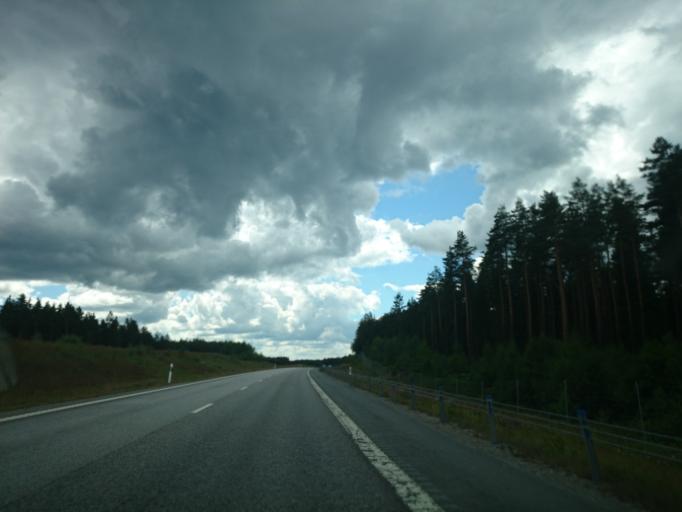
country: SE
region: Uppsala
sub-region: Tierps Kommun
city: Tierp
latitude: 60.2978
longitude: 17.5171
